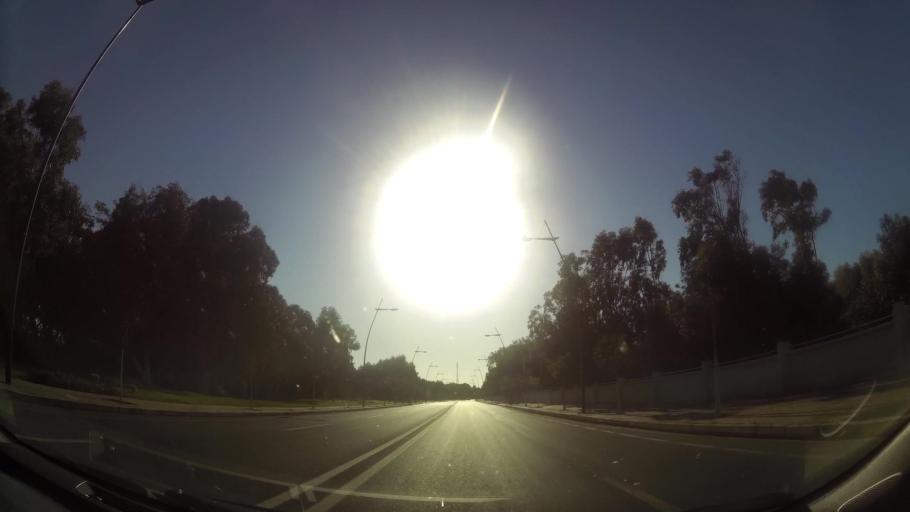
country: MA
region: Oriental
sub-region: Berkane-Taourirt
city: Madagh
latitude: 35.0901
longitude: -2.2473
